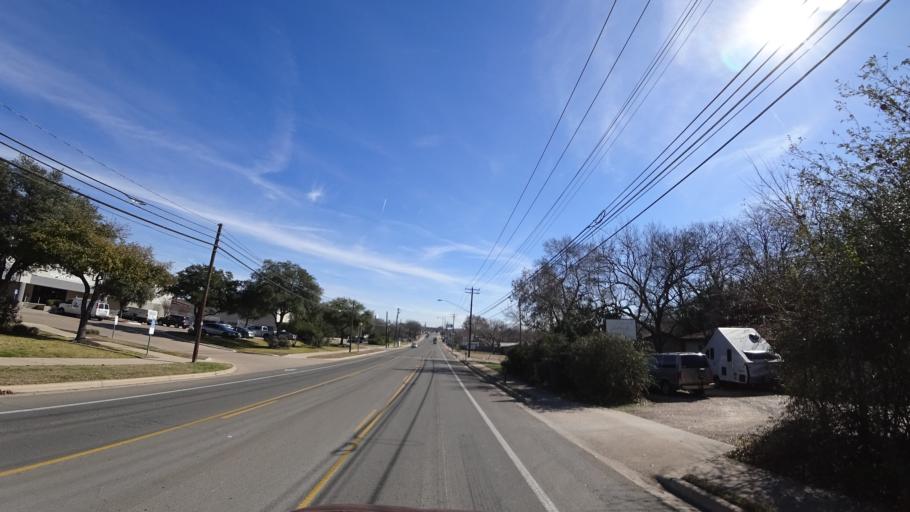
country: US
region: Texas
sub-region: Travis County
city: Wells Branch
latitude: 30.3818
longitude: -97.6924
